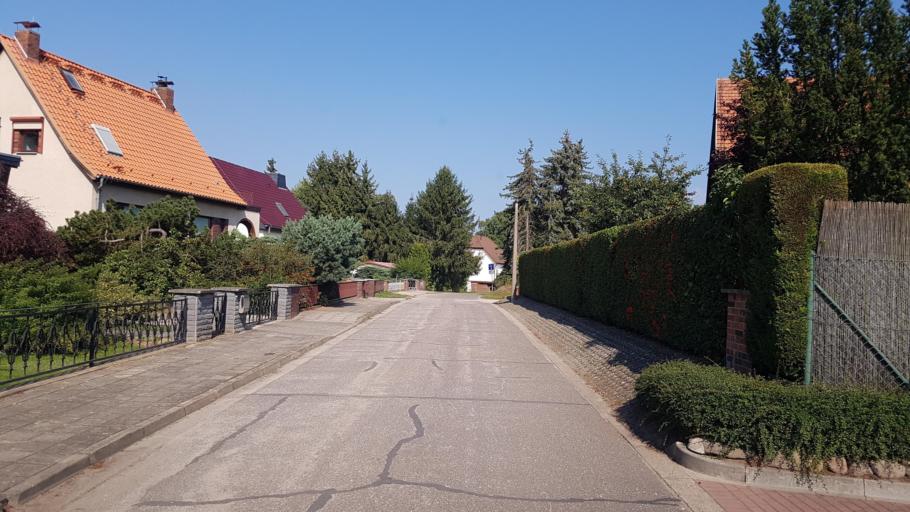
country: DE
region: Brandenburg
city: Vetschau
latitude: 51.7904
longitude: 14.0700
